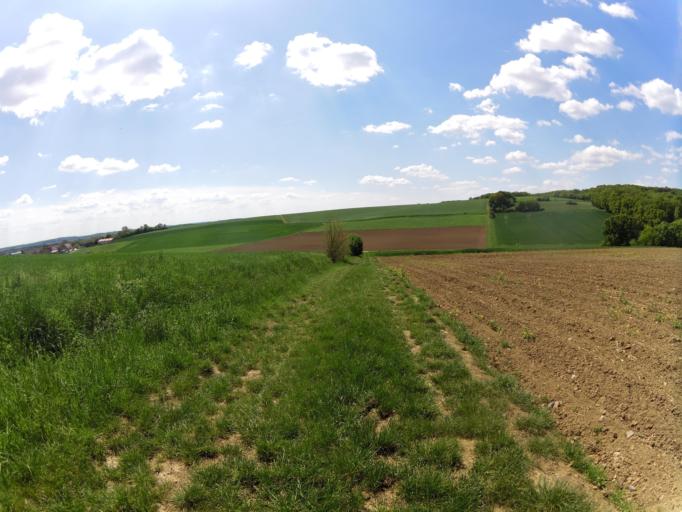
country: DE
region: Bavaria
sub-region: Regierungsbezirk Unterfranken
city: Unterpleichfeld
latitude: 49.8877
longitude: 10.0055
